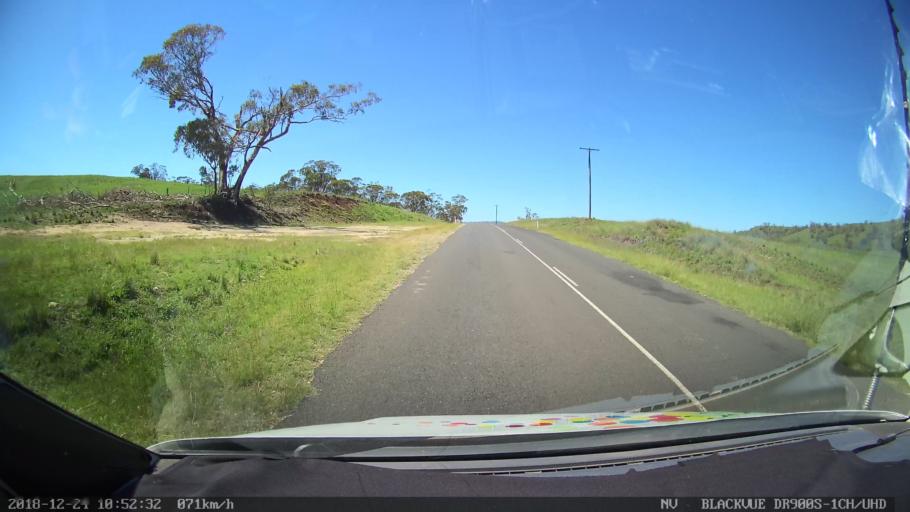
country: AU
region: New South Wales
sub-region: Upper Hunter Shire
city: Merriwa
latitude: -31.9817
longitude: 150.4222
